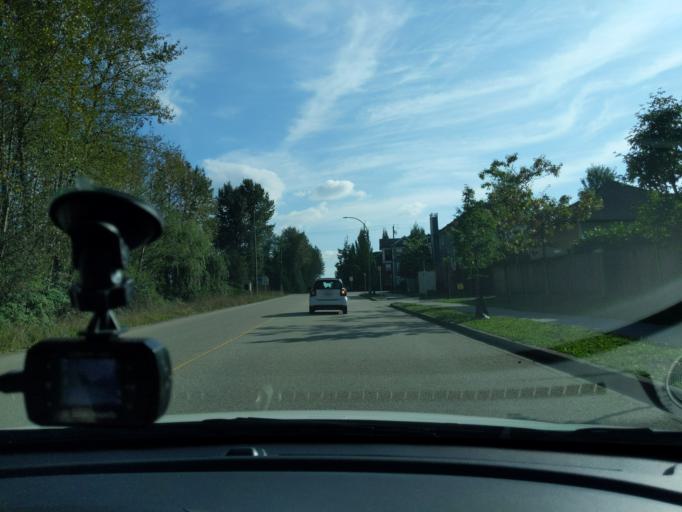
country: CA
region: British Columbia
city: Pitt Meadows
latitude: 49.2036
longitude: -122.6783
